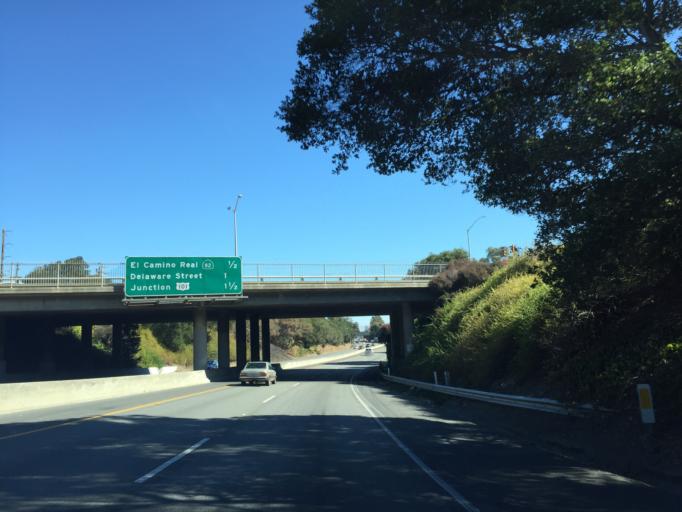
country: US
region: California
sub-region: San Mateo County
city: San Mateo
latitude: 37.5469
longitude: -122.3235
